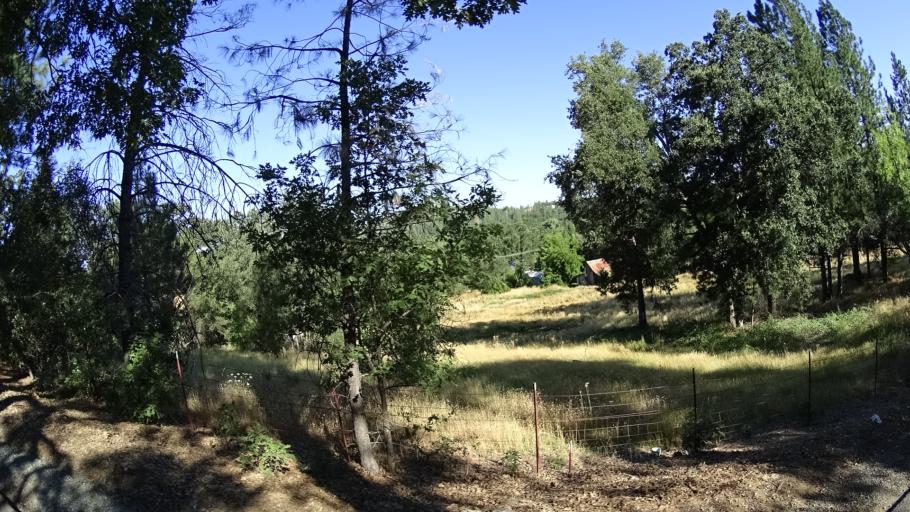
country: US
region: California
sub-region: Calaveras County
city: Murphys
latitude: 38.1351
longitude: -120.4586
